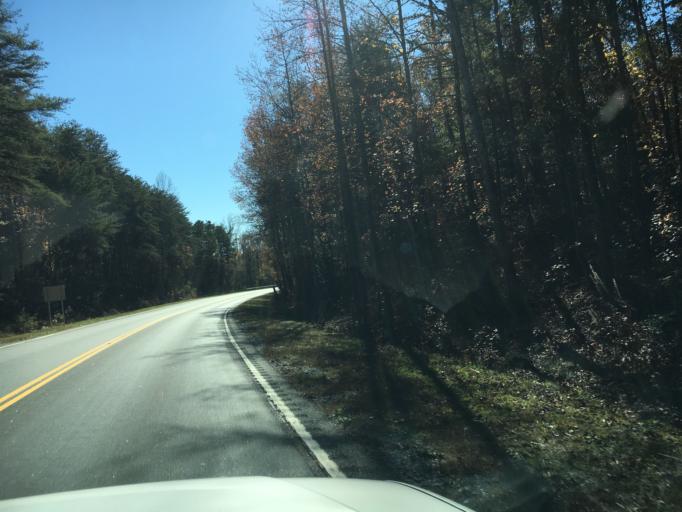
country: US
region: Georgia
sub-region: Hart County
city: Hartwell
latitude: 34.3584
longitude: -82.8134
